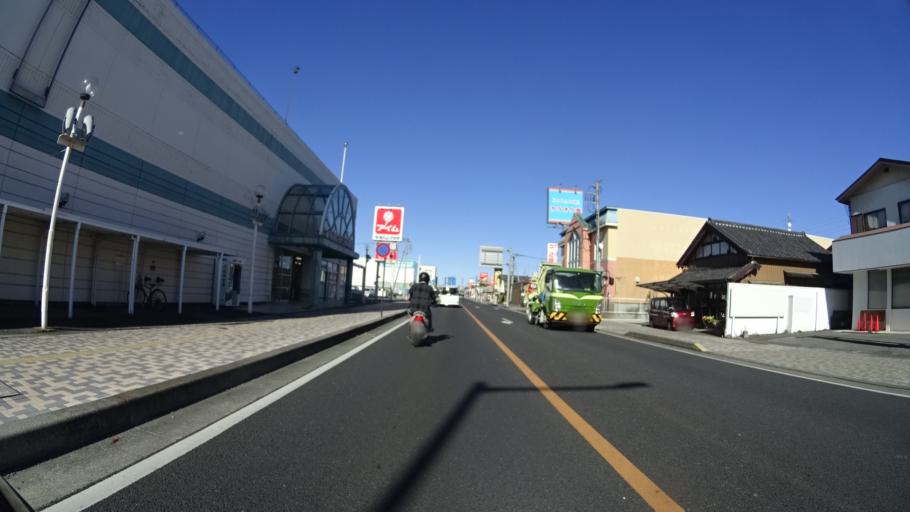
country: JP
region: Tochigi
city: Tochigi
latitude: 36.3904
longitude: 139.7362
